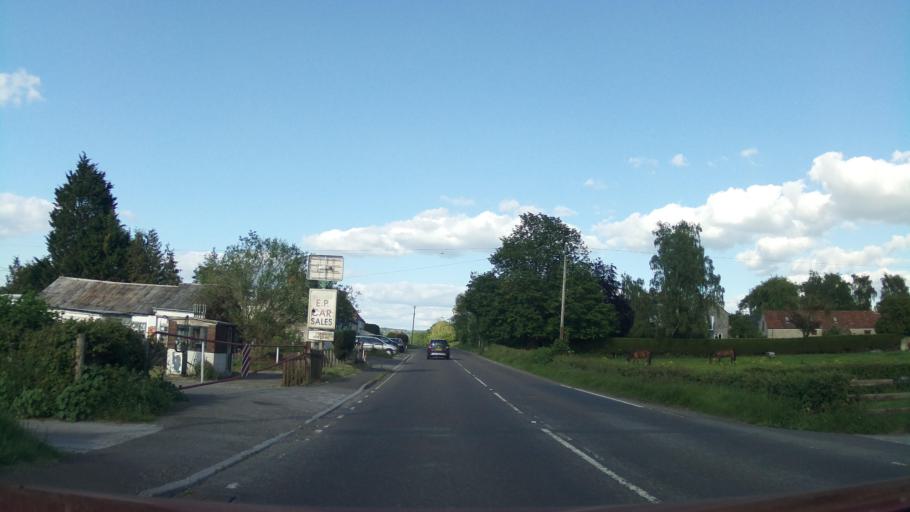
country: GB
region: England
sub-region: Somerset
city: Wells
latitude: 51.1513
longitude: -2.6288
